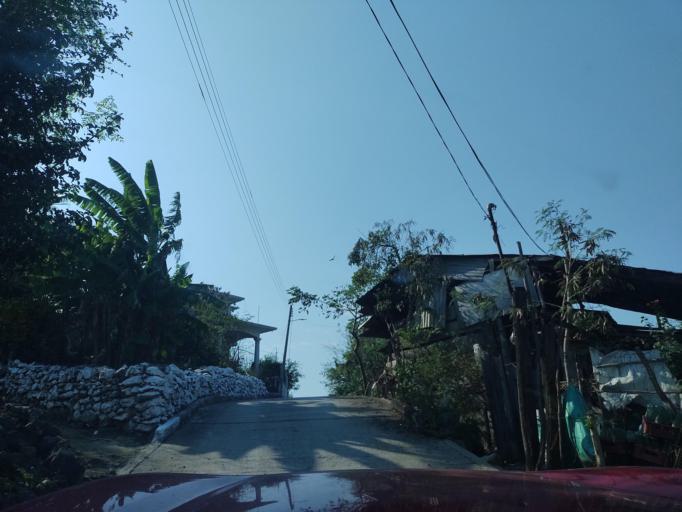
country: MX
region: Veracruz
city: Agua Dulce
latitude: 20.3692
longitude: -97.1844
